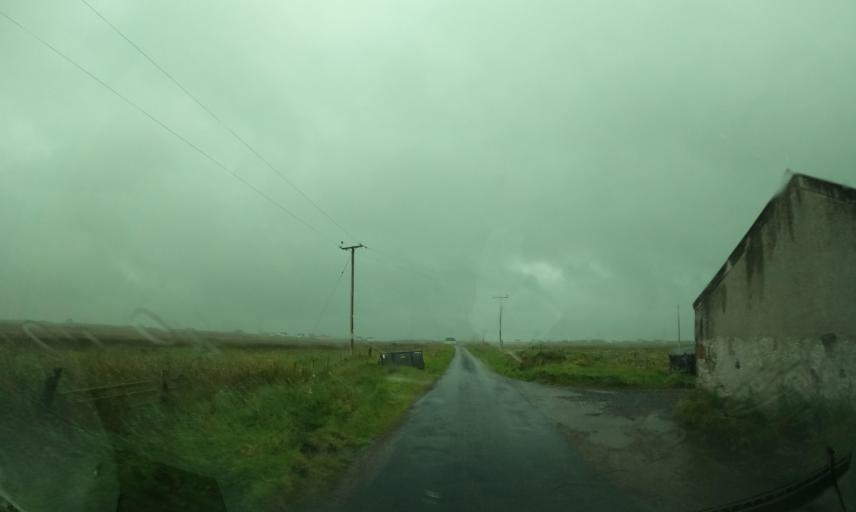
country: GB
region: Scotland
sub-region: Eilean Siar
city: Barra
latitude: 56.4683
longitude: -6.9091
